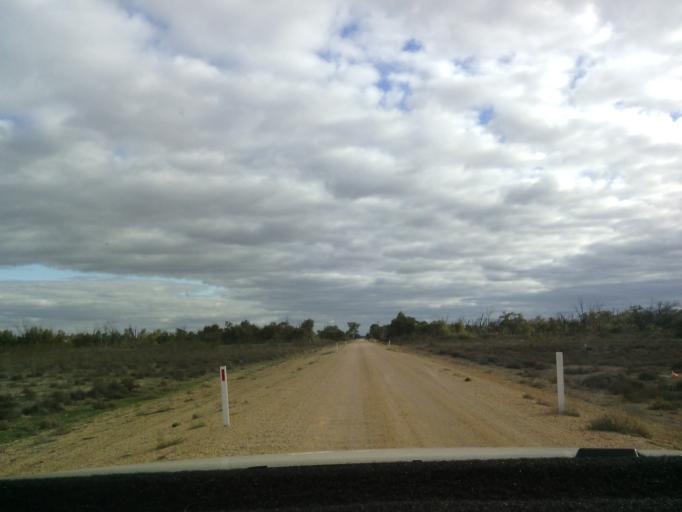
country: AU
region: South Australia
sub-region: Renmark Paringa
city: Renmark
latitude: -34.1647
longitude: 141.1936
